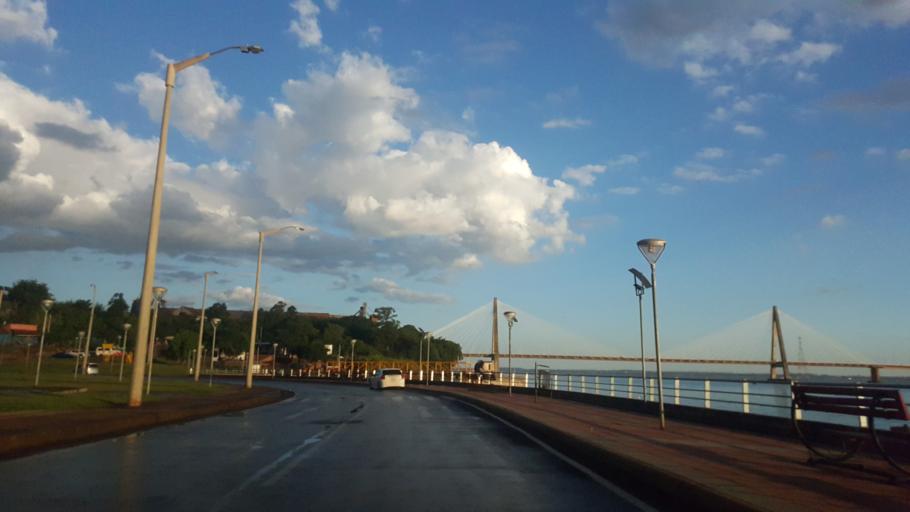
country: PY
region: Itapua
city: Encarnacion
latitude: -27.3619
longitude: -55.8628
